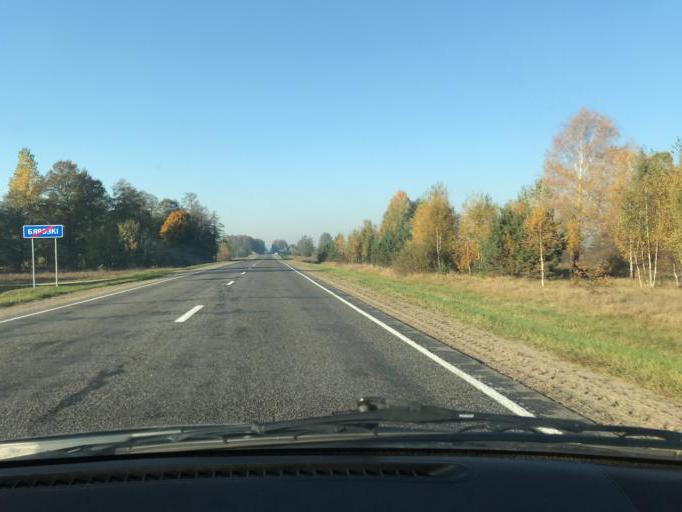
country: BY
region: Brest
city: Baranovichi
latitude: 52.9209
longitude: 25.9811
